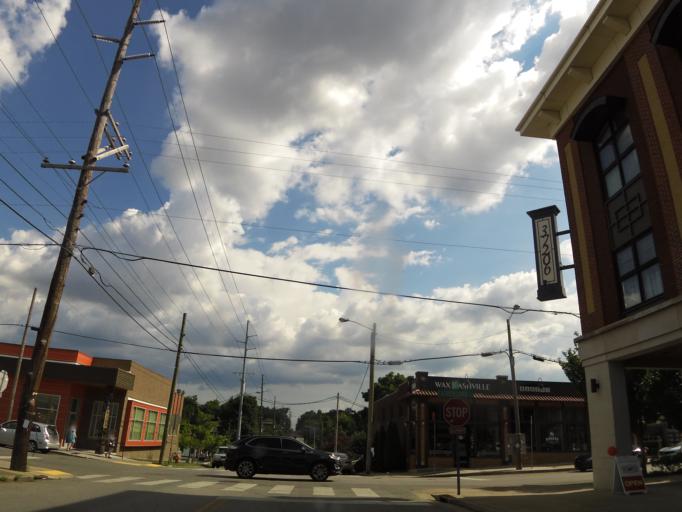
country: US
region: Tennessee
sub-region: Davidson County
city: Nashville
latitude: 36.1744
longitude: -86.7504
